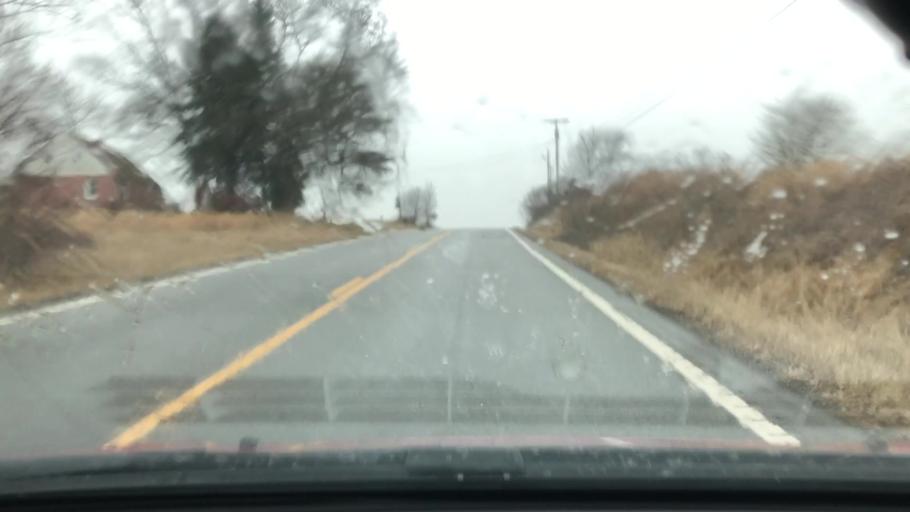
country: US
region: Ohio
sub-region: Wayne County
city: Rittman
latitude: 40.9390
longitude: -81.7482
